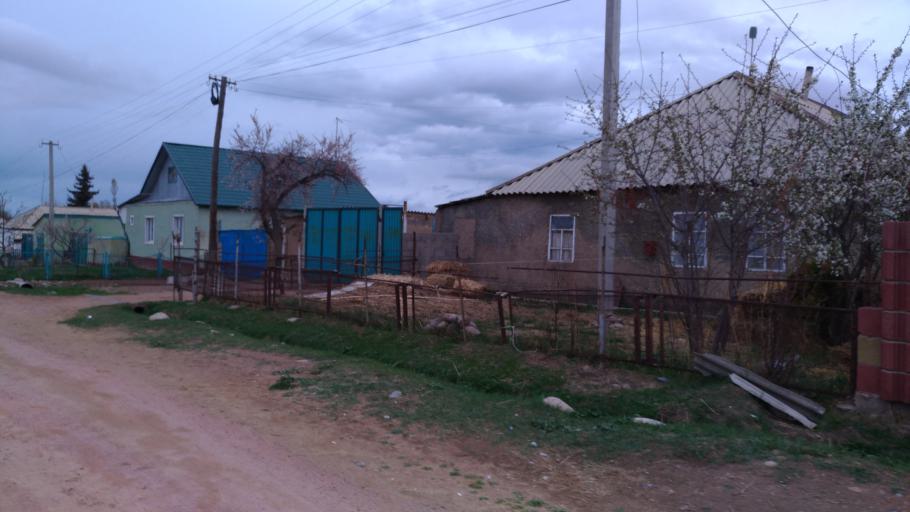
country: KG
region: Ysyk-Koel
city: Bokombayevskoye
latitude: 42.1133
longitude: 76.9835
